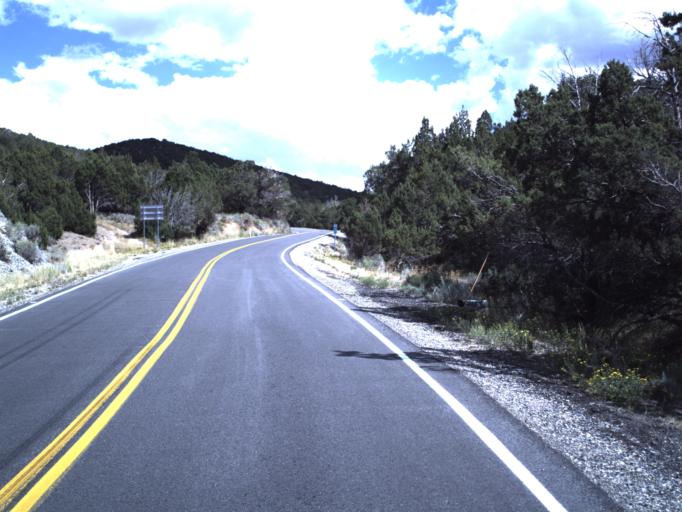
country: US
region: Utah
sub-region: Tooele County
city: Grantsville
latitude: 40.3457
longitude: -112.5878
